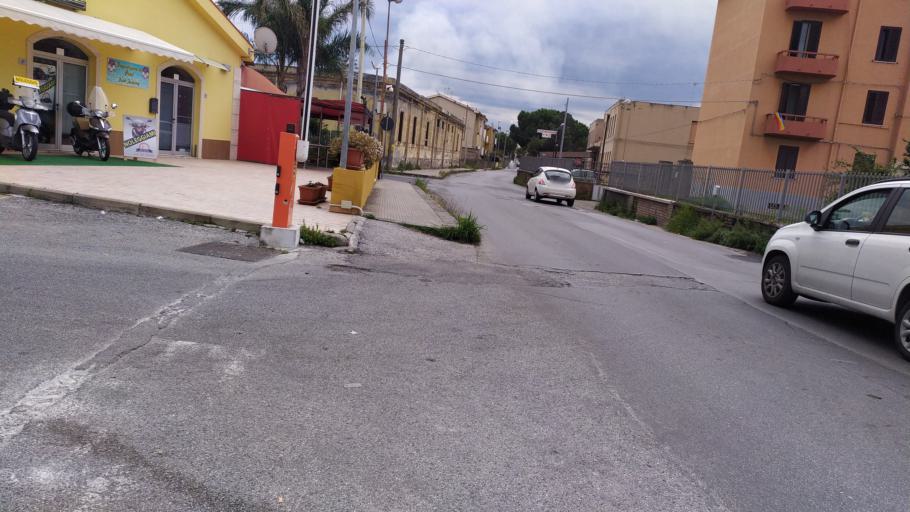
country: IT
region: Sicily
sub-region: Messina
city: Milazzo
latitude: 38.2130
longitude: 15.2417
